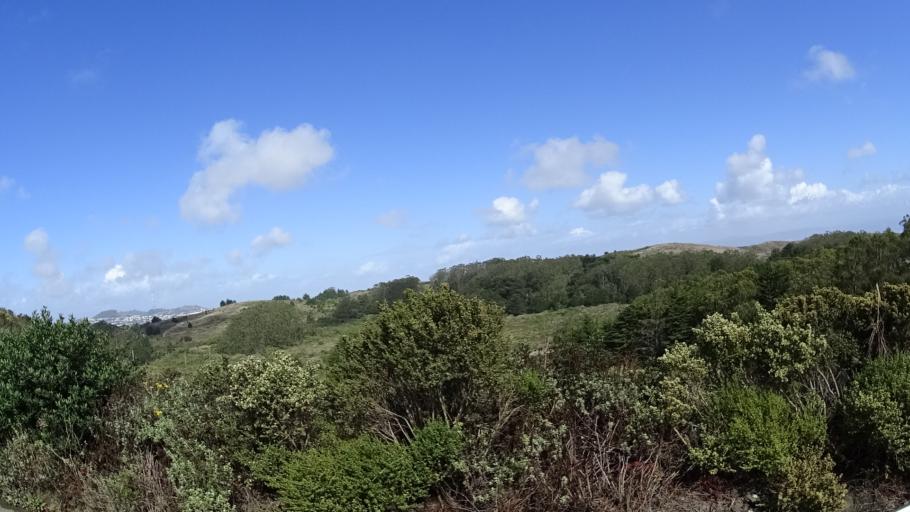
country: US
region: California
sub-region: San Mateo County
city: Daly City
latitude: 37.6946
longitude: -122.4391
